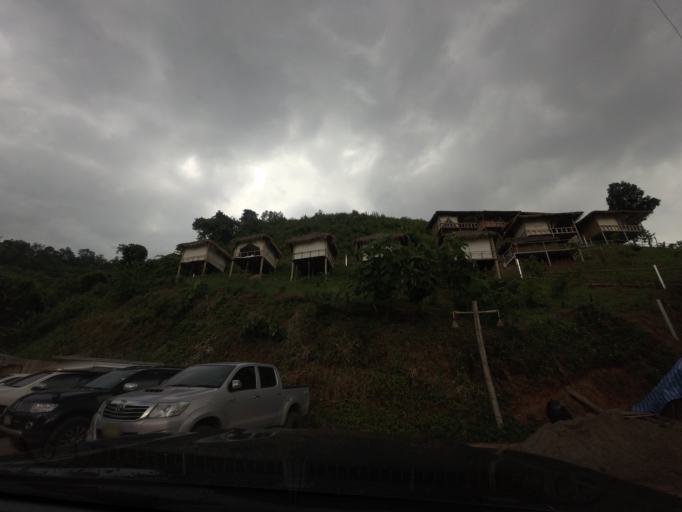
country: TH
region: Nan
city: Bo Kluea
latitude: 19.1957
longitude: 101.2022
